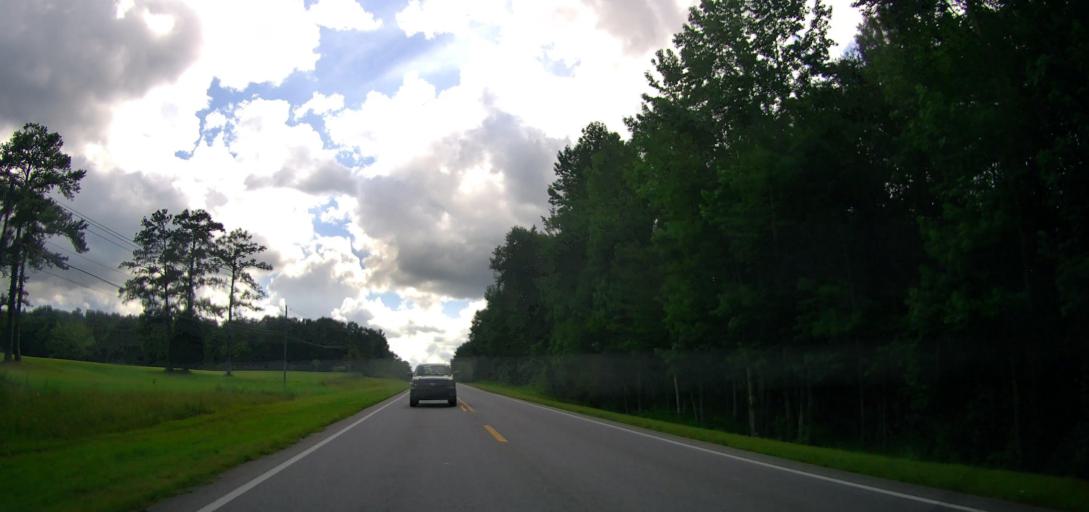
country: US
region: Alabama
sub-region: Russell County
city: Ladonia
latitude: 32.4605
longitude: -85.1743
